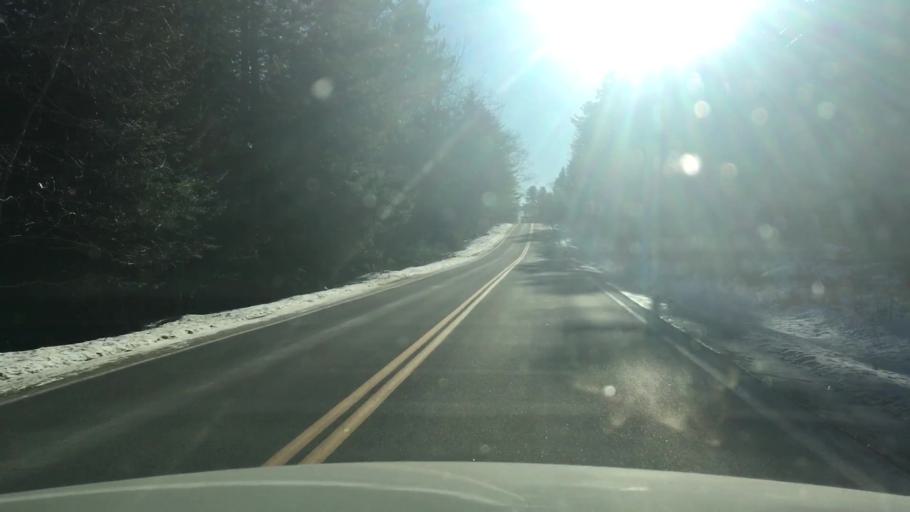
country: US
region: Maine
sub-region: Hancock County
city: Orland
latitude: 44.5166
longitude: -68.7511
